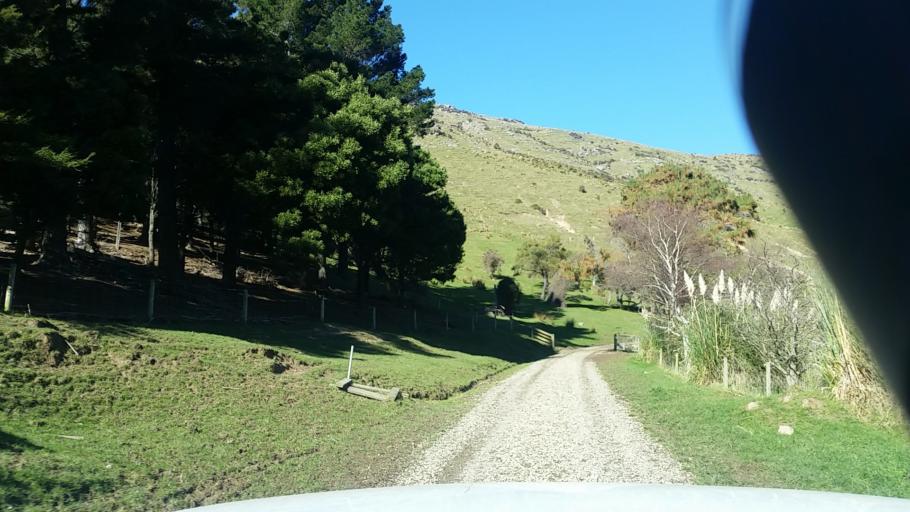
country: NZ
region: Canterbury
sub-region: Christchurch City
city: Christchurch
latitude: -43.6527
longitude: 172.9572
